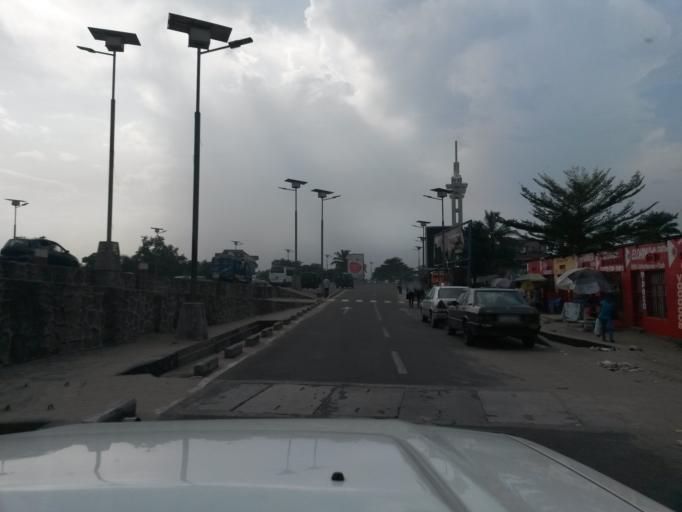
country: CD
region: Kinshasa
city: Masina
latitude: -4.3797
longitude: 15.3494
